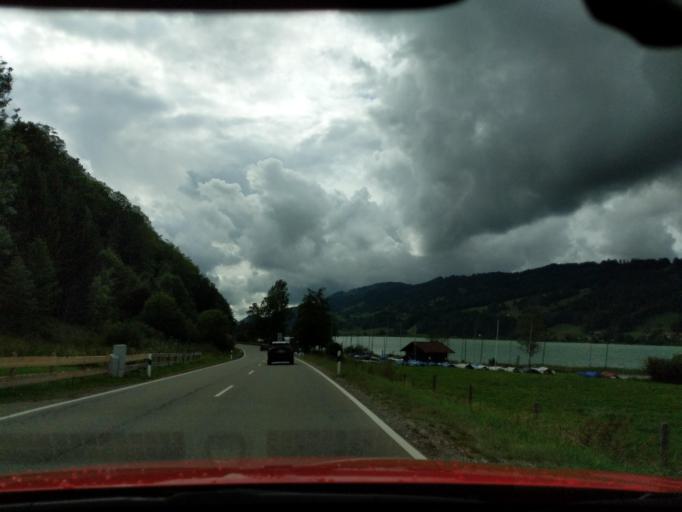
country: DE
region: Bavaria
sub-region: Swabia
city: Immenstadt im Allgau
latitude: 47.5678
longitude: 10.1724
